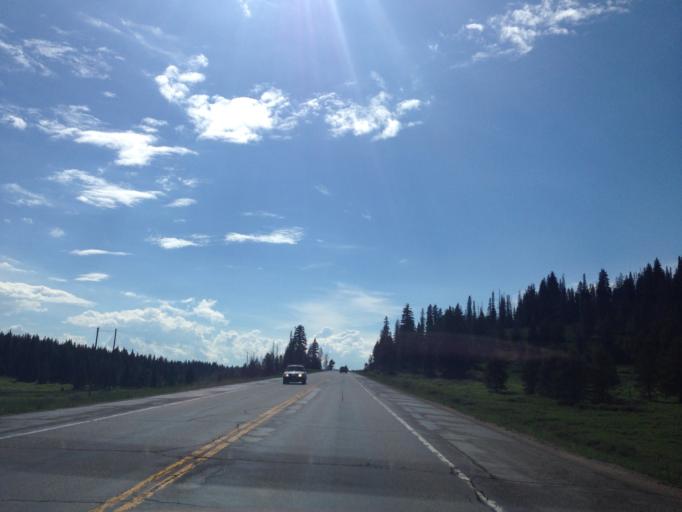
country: US
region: Colorado
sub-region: Routt County
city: Steamboat Springs
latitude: 40.3889
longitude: -106.6388
